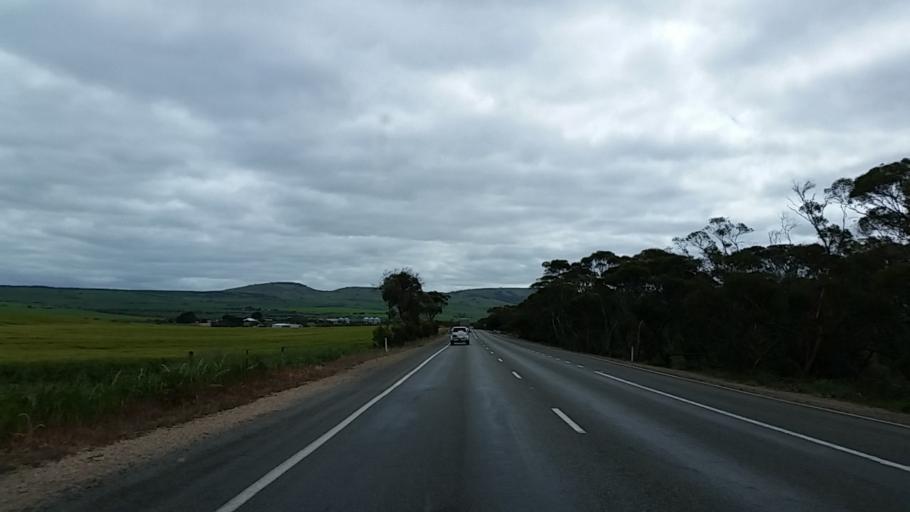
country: AU
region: South Australia
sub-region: Wakefield
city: Balaklava
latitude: -33.9581
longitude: 138.1759
